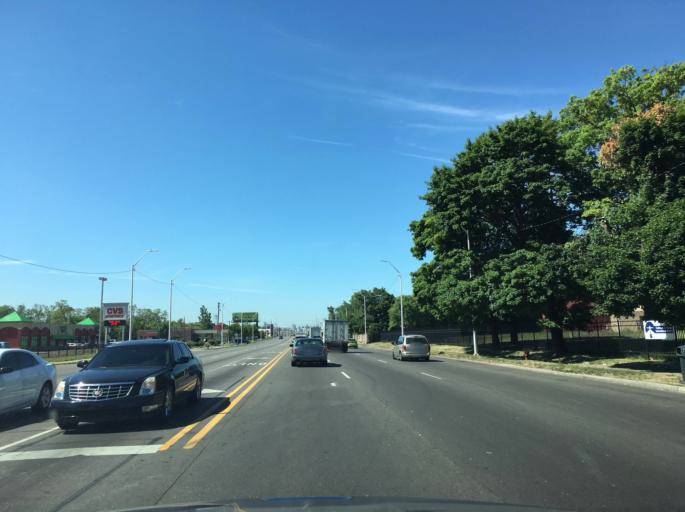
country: US
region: Michigan
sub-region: Wayne County
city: Hamtramck
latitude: 42.4048
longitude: -82.9976
